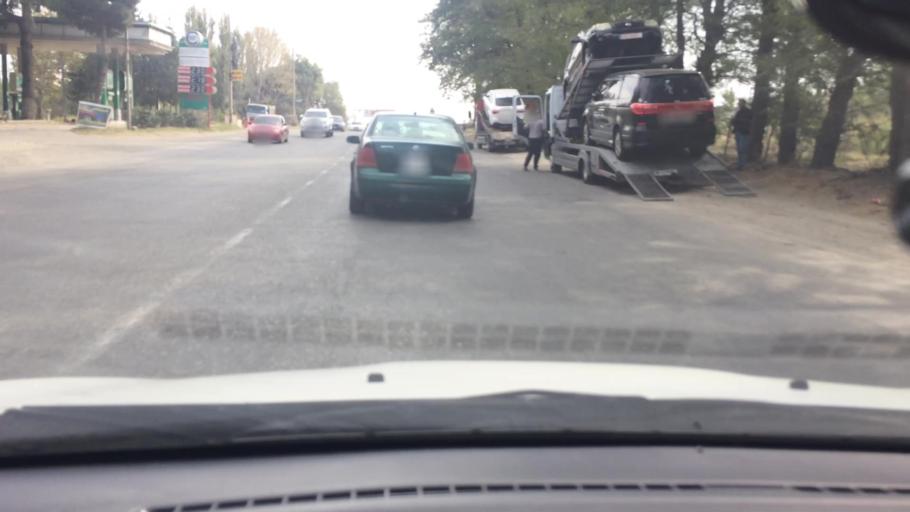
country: GE
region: T'bilisi
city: Tbilisi
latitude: 41.6418
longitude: 44.9136
